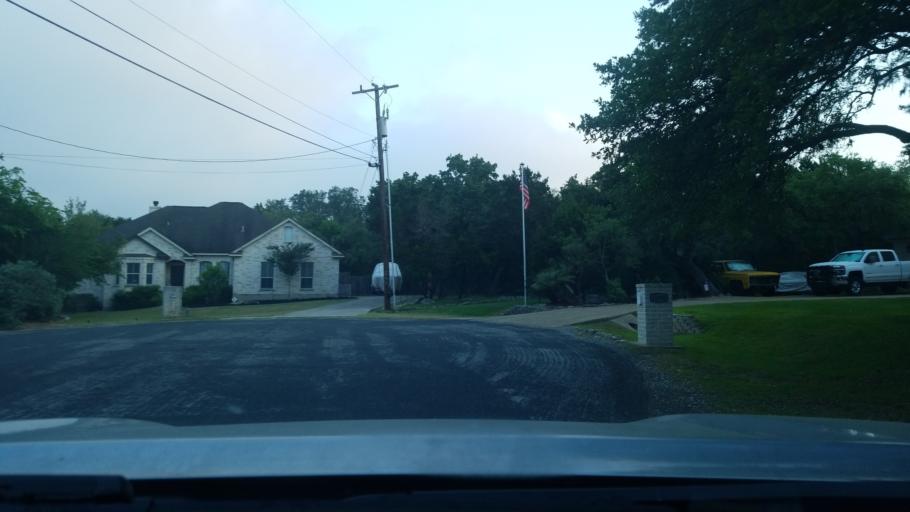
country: US
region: Texas
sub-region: Bexar County
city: Timberwood Park
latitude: 29.6981
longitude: -98.5047
